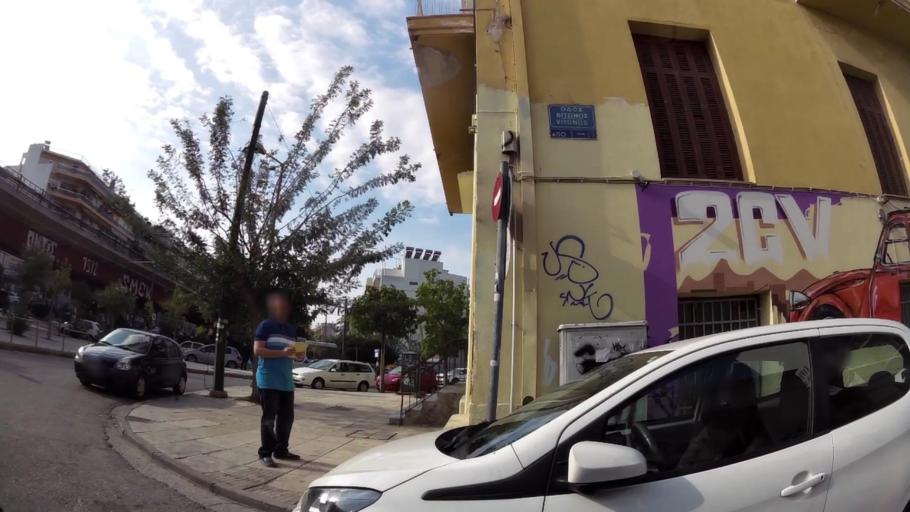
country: GR
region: Attica
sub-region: Nomarchia Athinas
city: Athens
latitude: 37.9762
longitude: 23.7136
